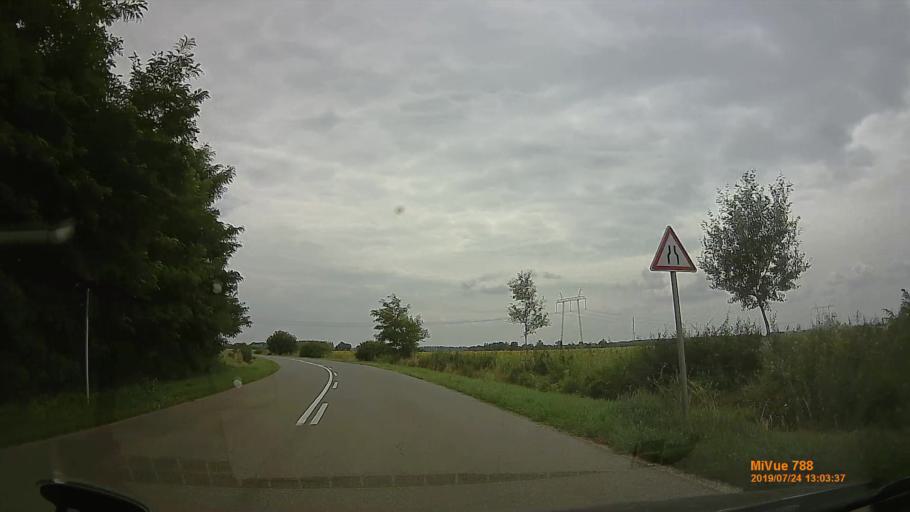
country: HU
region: Szabolcs-Szatmar-Bereg
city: Aranyosapati
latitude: 48.2099
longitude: 22.2996
